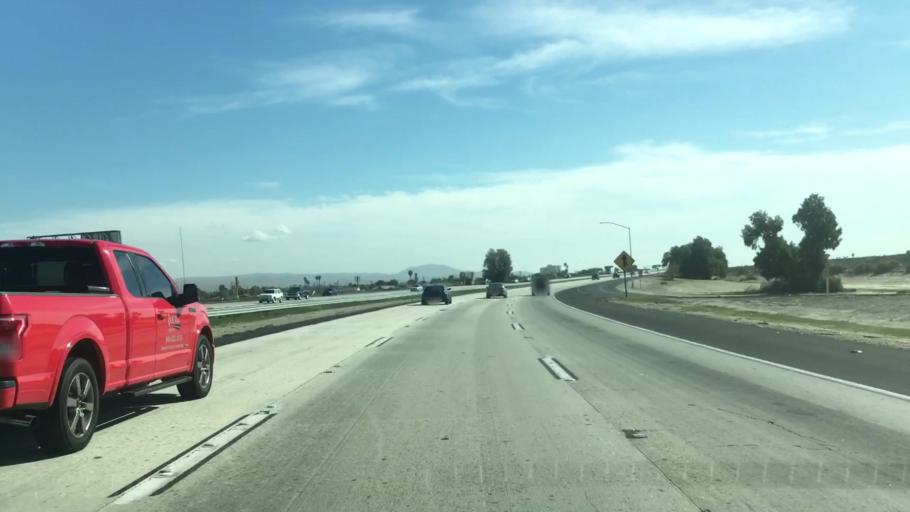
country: US
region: California
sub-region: Riverside County
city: Indio
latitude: 33.7365
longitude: -116.2141
